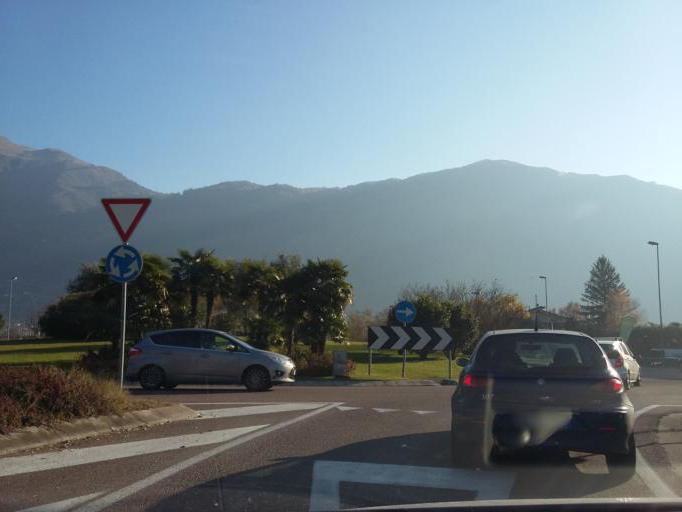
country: IT
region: Trentino-Alto Adige
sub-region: Provincia di Trento
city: Arco
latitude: 45.9090
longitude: 10.8789
